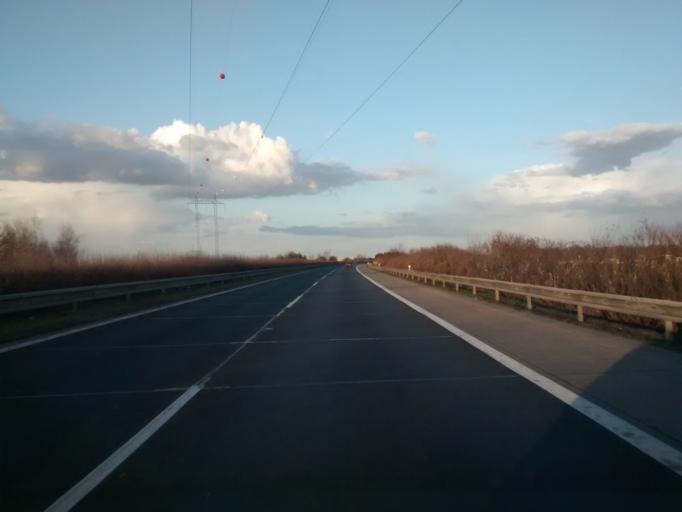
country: CZ
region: Central Bohemia
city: Sestajovice
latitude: 50.1174
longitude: 14.6686
